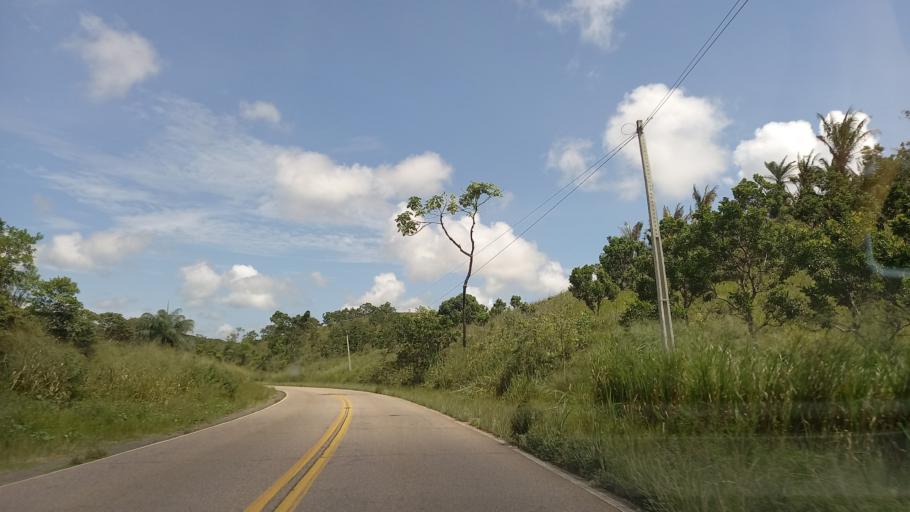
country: BR
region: Pernambuco
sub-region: Barreiros
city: Barreiros
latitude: -8.7685
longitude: -35.1715
